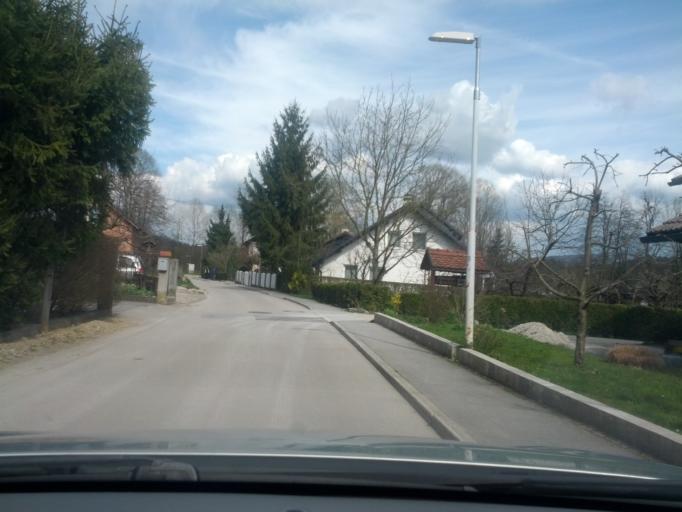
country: SI
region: Dol pri Ljubljani
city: Dol pri Ljubljani
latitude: 46.1096
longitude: 14.5961
